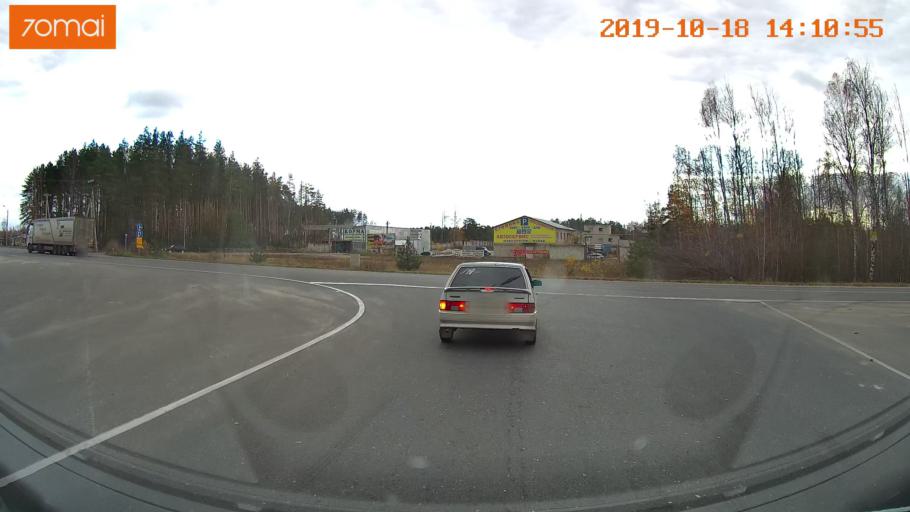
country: RU
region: Rjazan
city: Spas-Klepiki
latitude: 55.1396
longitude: 40.2172
